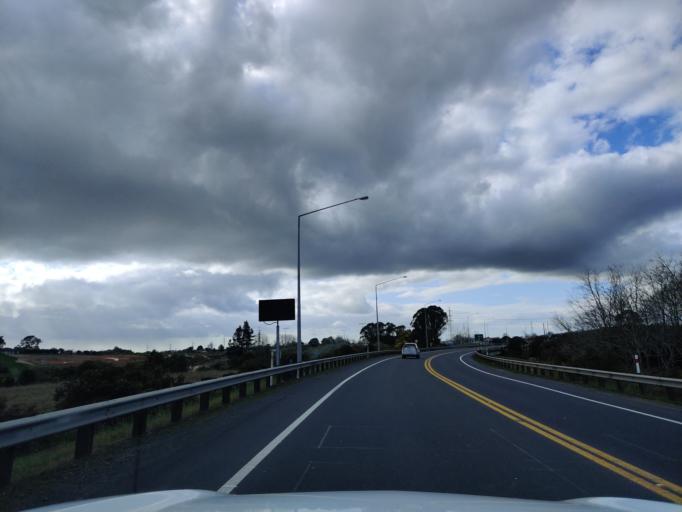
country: NZ
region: Auckland
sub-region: Auckland
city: Papakura
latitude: -37.1110
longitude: 174.9425
